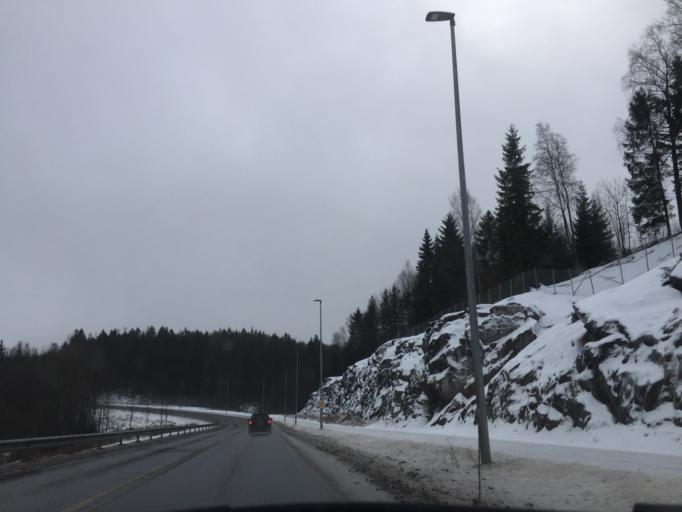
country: NO
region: Akershus
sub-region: Frogn
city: Drobak
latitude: 59.6658
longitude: 10.6601
